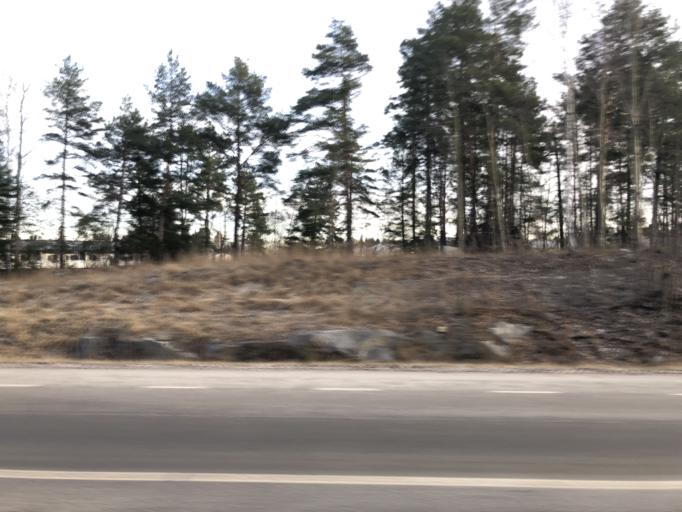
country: SE
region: Stockholm
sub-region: Jarfalla Kommun
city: Jakobsberg
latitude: 59.4041
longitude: 17.7968
